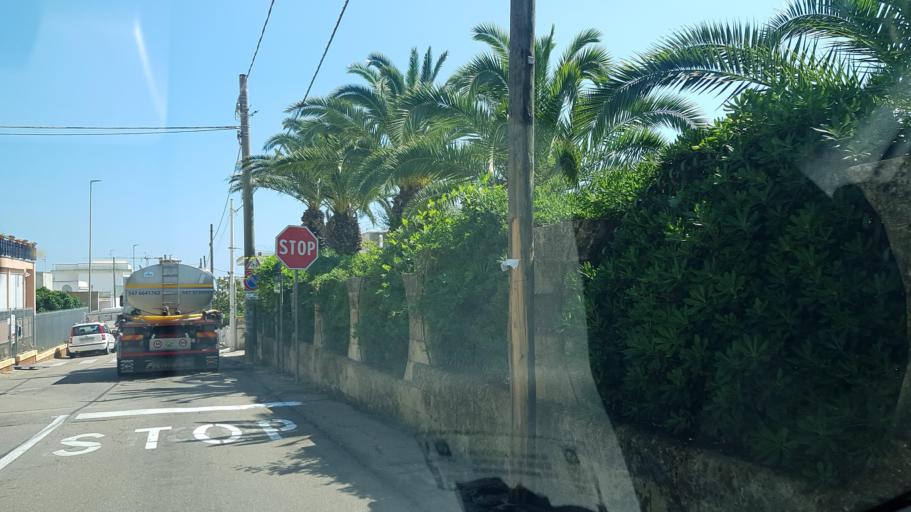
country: IT
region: Apulia
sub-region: Provincia di Lecce
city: Leuca
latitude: 39.8012
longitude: 18.3538
